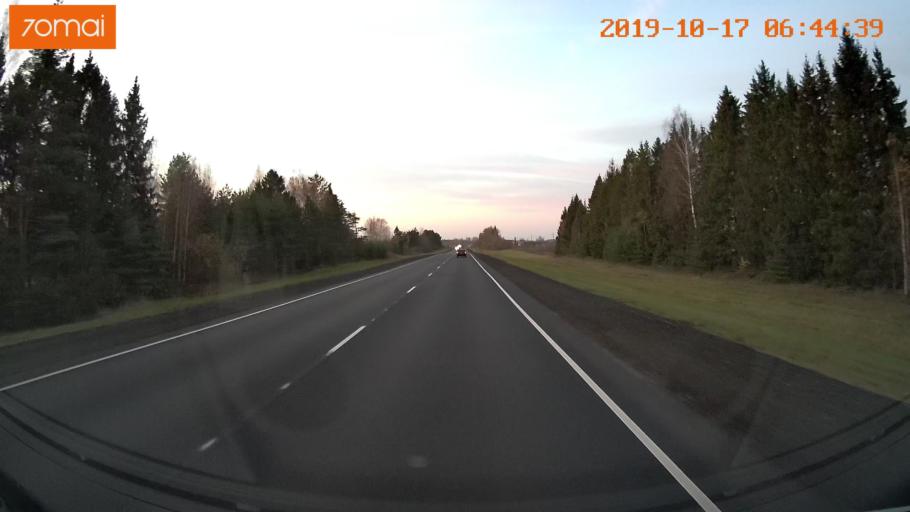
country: RU
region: Vladimir
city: Kideksha
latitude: 56.5693
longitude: 40.5530
